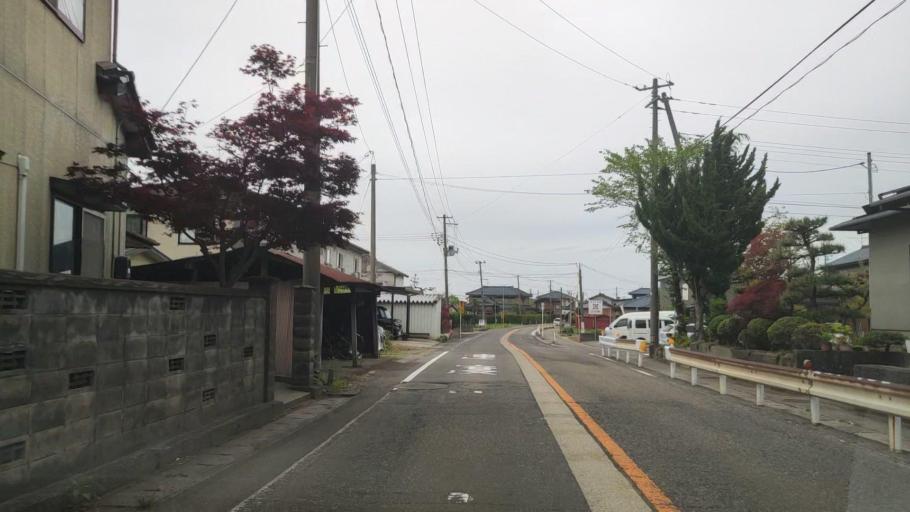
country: JP
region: Niigata
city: Kamo
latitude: 37.7145
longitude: 139.0734
